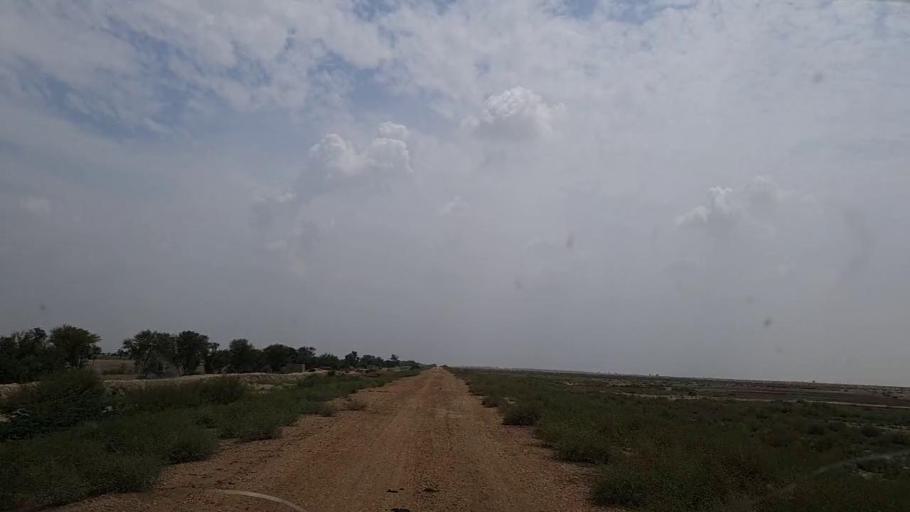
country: PK
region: Sindh
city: Johi
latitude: 26.7993
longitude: 67.6026
